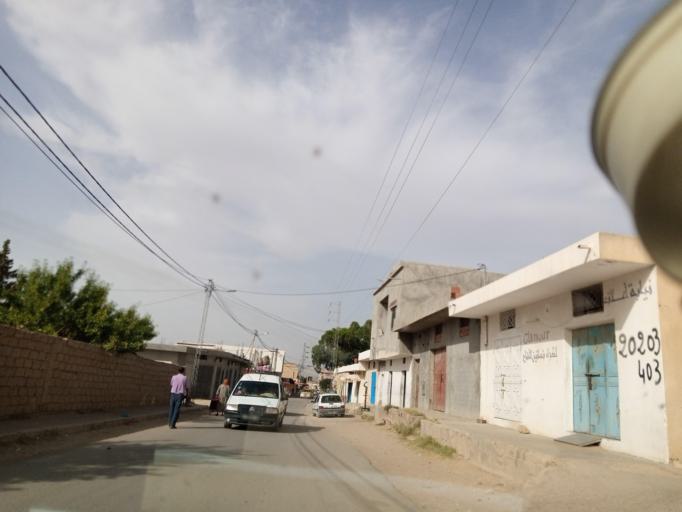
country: TN
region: Al Qasrayn
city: Kasserine
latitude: 35.2135
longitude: 8.8967
